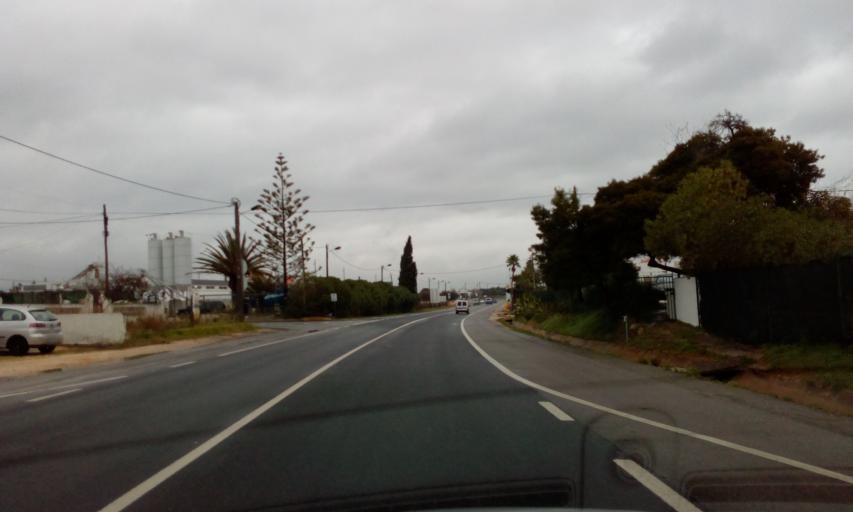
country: PT
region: Faro
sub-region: Lagos
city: Lagos
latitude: 37.1430
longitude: -8.6621
